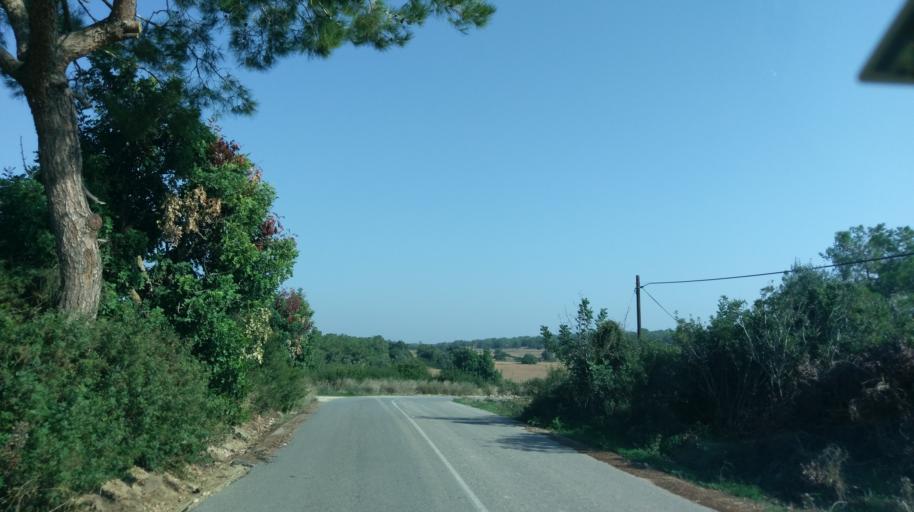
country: CY
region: Ammochostos
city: Leonarisso
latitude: 35.4768
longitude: 34.1915
